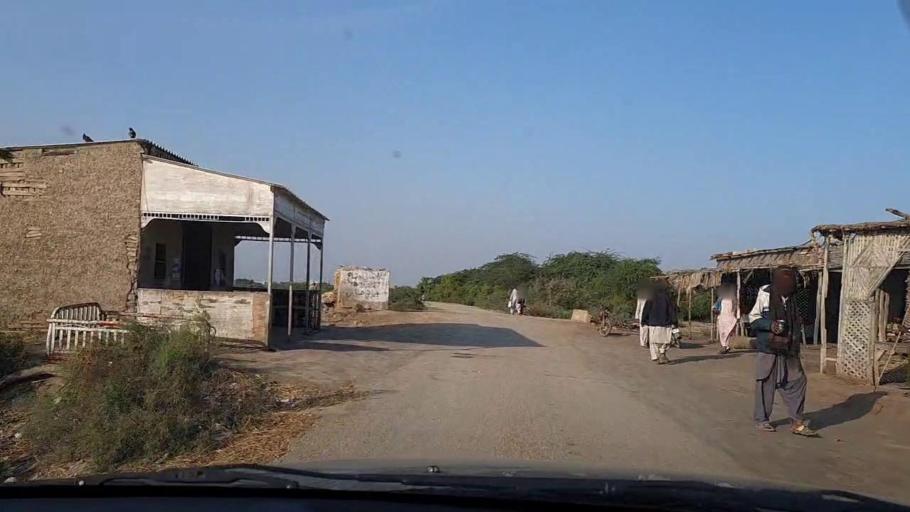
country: PK
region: Sindh
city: Chuhar Jamali
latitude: 24.2997
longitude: 67.7555
